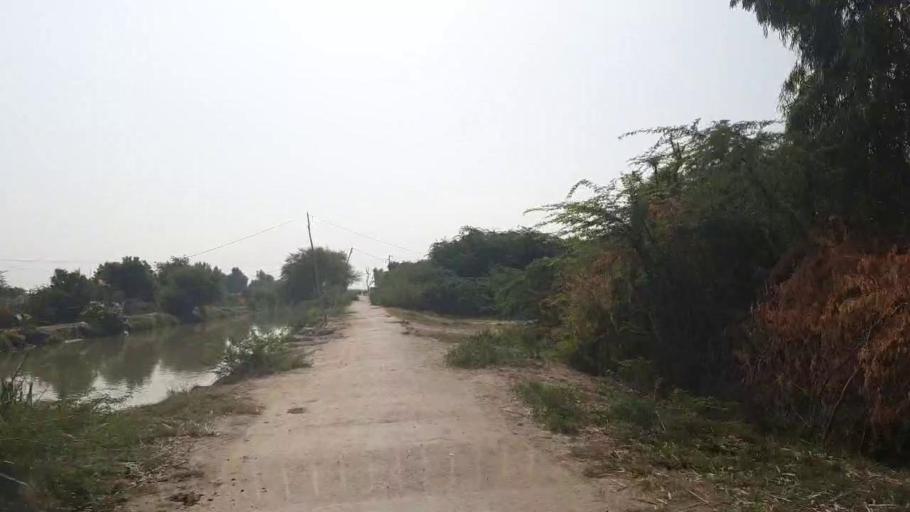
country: PK
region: Sindh
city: Badin
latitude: 24.6393
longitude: 68.8495
